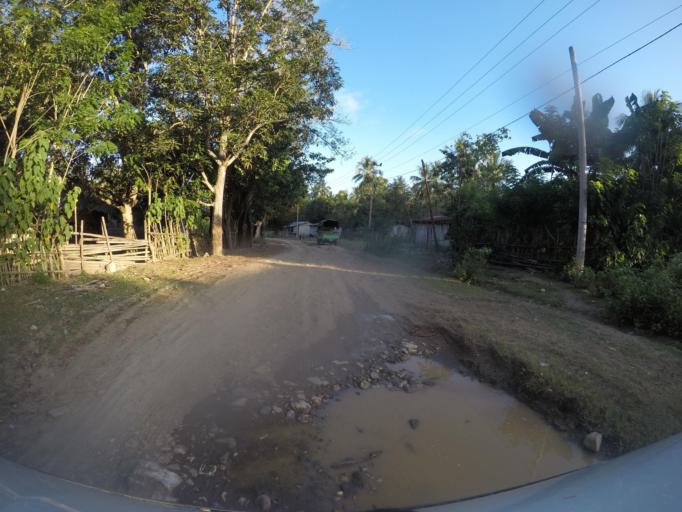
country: TL
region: Baucau
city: Venilale
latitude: -8.7321
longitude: 126.7094
